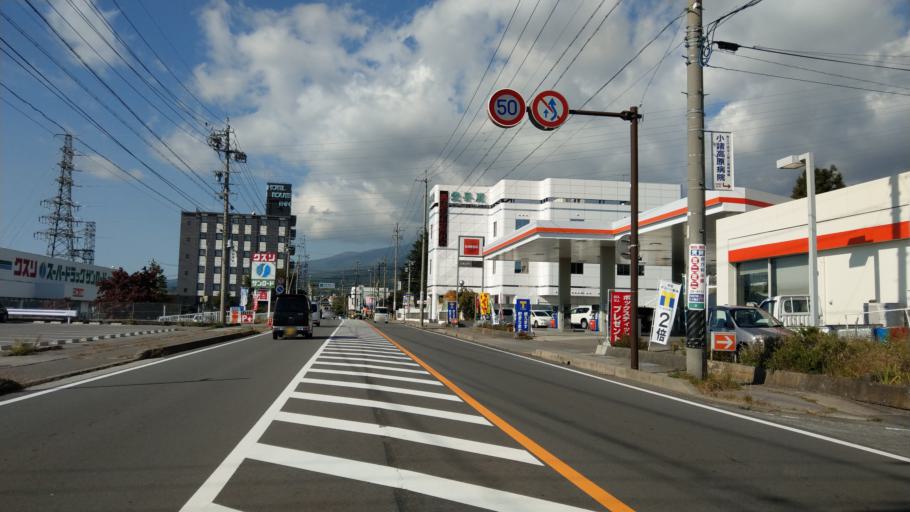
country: JP
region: Nagano
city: Komoro
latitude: 36.3275
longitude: 138.4343
